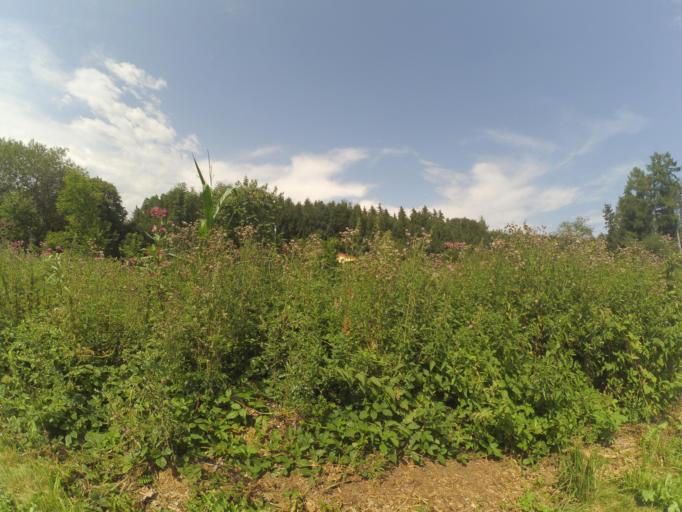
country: DE
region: Bavaria
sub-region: Swabia
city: Buchloe
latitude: 48.0265
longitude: 10.7358
